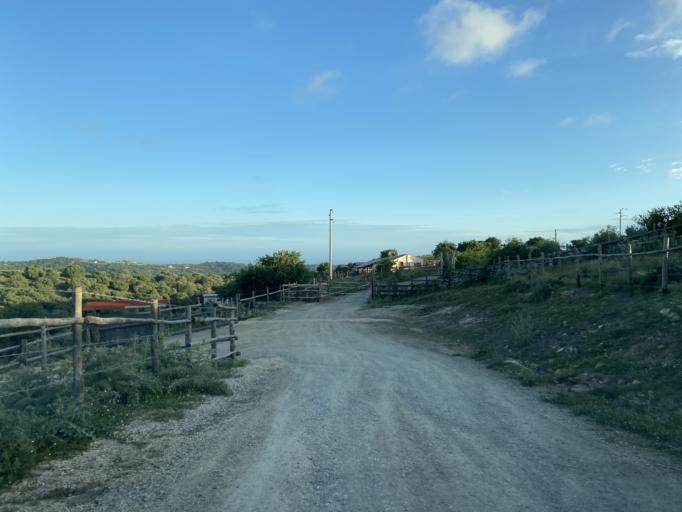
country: IT
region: Latium
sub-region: Citta metropolitana di Roma Capitale
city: Santa Marinella
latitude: 42.0822
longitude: 11.8511
